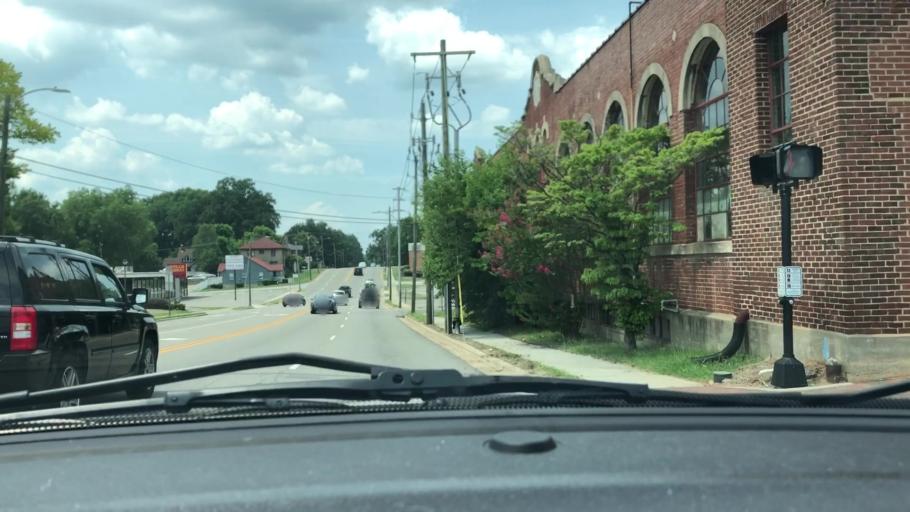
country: US
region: North Carolina
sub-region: Lee County
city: Sanford
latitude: 35.4800
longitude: -79.1805
